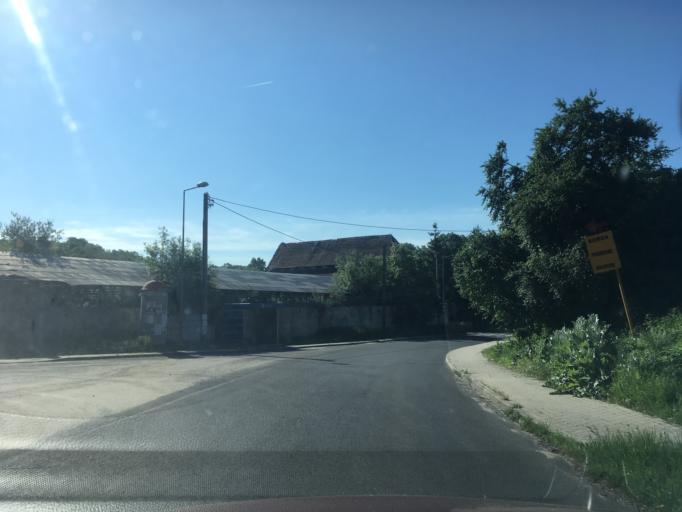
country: PL
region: Lower Silesian Voivodeship
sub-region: Powiat zgorzelecki
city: Zgorzelec
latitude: 51.1179
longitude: 15.0262
